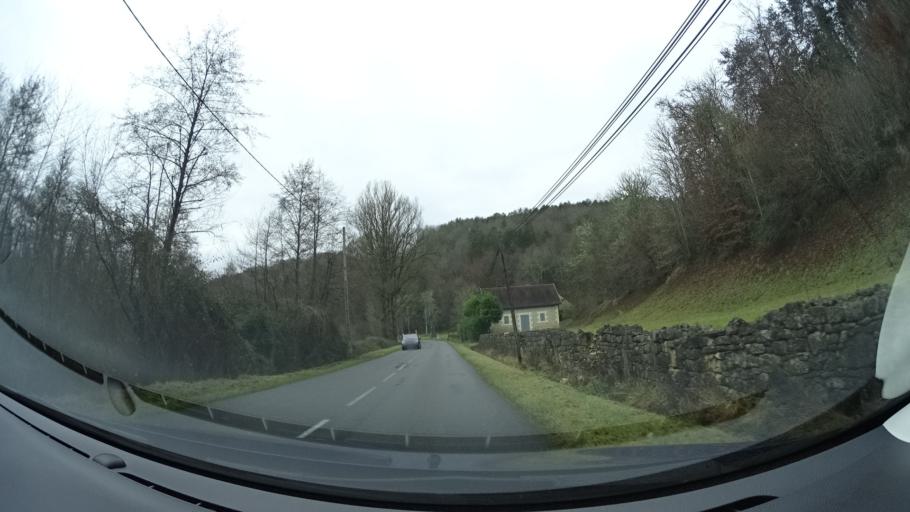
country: FR
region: Aquitaine
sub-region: Departement de la Dordogne
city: Saint-Cyprien
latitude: 44.8793
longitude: 1.0616
